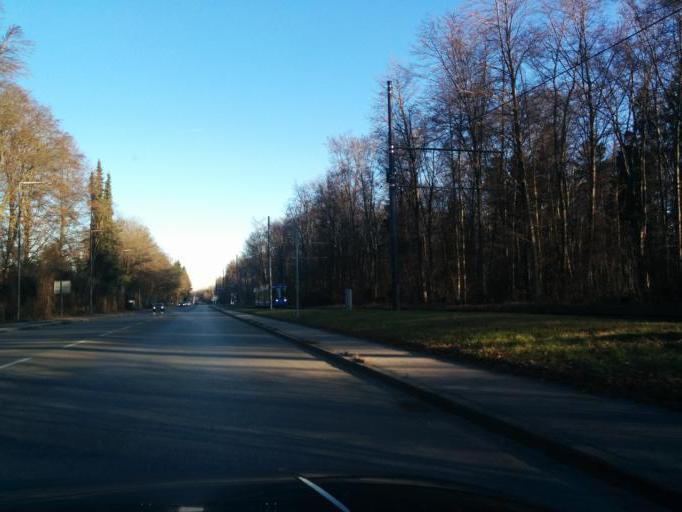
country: DE
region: Bavaria
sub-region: Upper Bavaria
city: Pullach im Isartal
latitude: 48.0691
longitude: 11.5461
